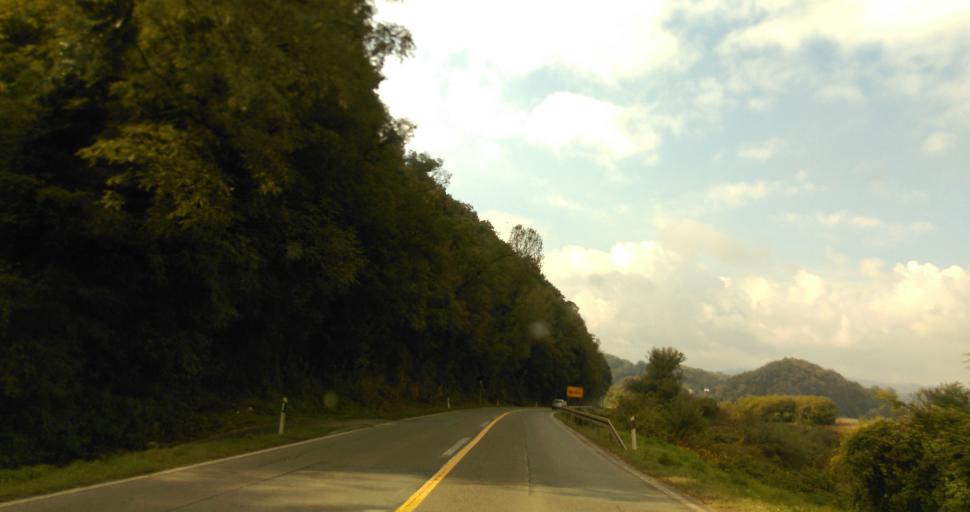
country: RS
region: Central Serbia
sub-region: Kolubarski Okrug
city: Ljig
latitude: 44.2359
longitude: 20.2619
